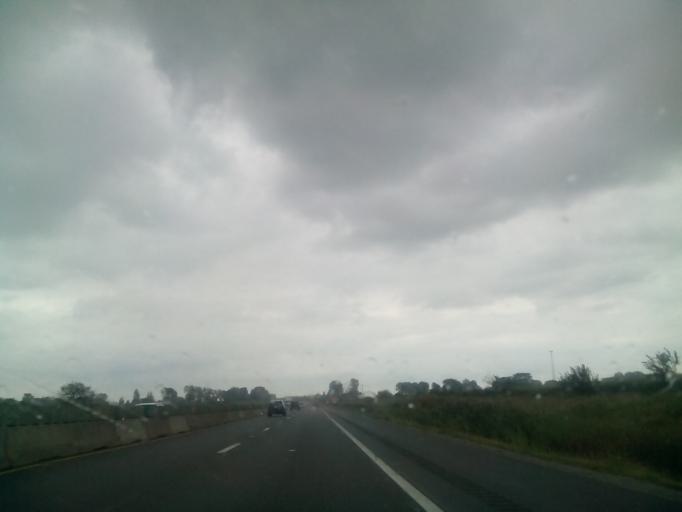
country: US
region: Ohio
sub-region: Huron County
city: Bellevue
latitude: 41.3558
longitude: -82.8866
